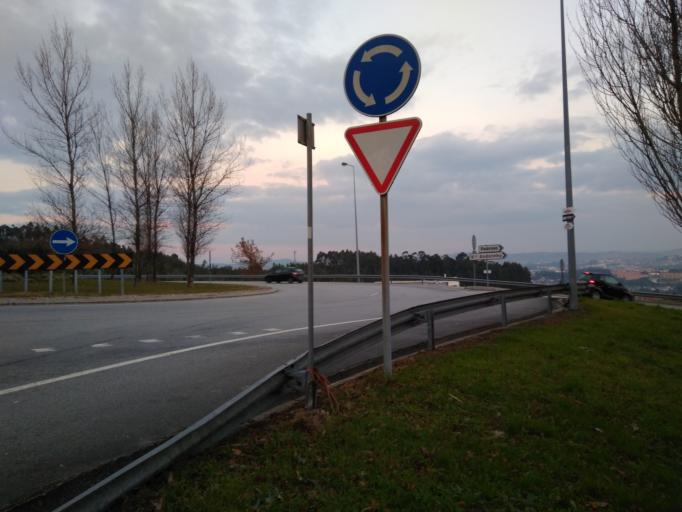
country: PT
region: Porto
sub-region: Vila Nova de Gaia
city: Vilar de Andorinho
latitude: 41.0993
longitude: -8.5846
